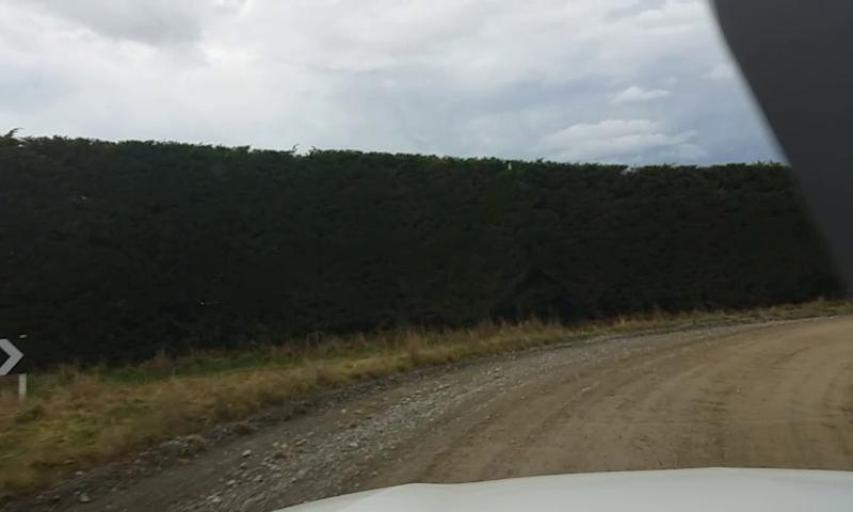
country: NZ
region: Canterbury
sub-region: Waimakariri District
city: Kaiapoi
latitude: -43.2908
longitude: 172.4465
